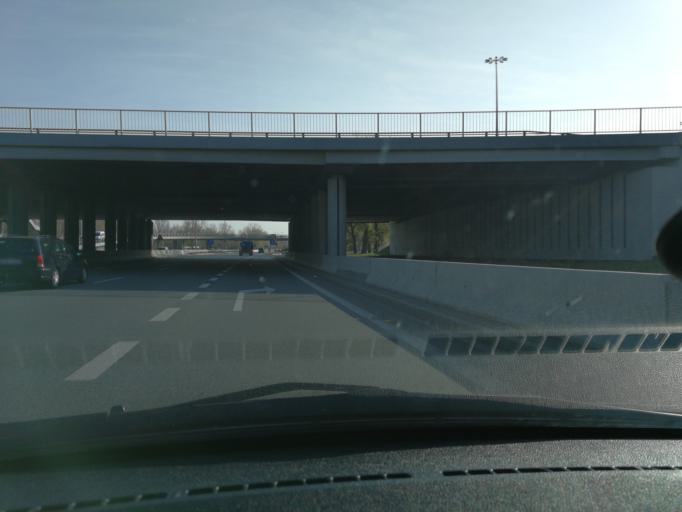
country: PL
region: Masovian Voivodeship
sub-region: Warszawa
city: Zoliborz
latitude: 52.2846
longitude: 20.9881
